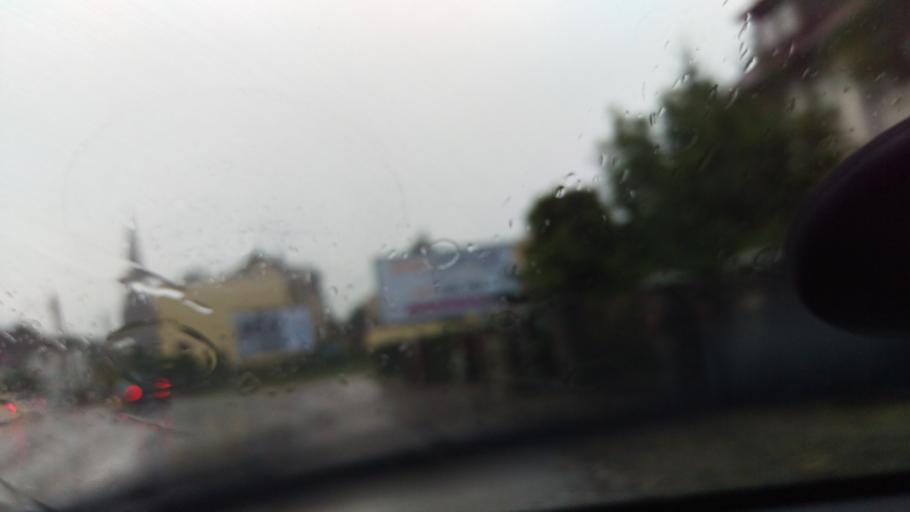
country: PL
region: West Pomeranian Voivodeship
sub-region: Szczecin
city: Szczecin
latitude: 53.3925
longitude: 14.6628
